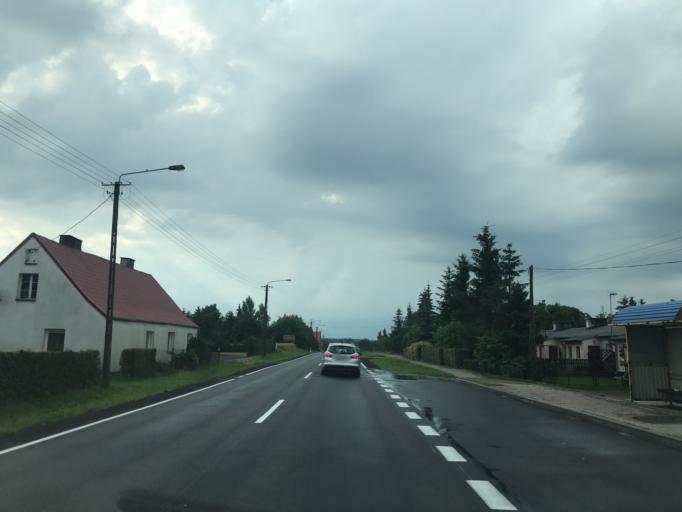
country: PL
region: Pomeranian Voivodeship
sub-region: Powiat czluchowski
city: Czluchow
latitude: 53.6780
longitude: 17.3409
